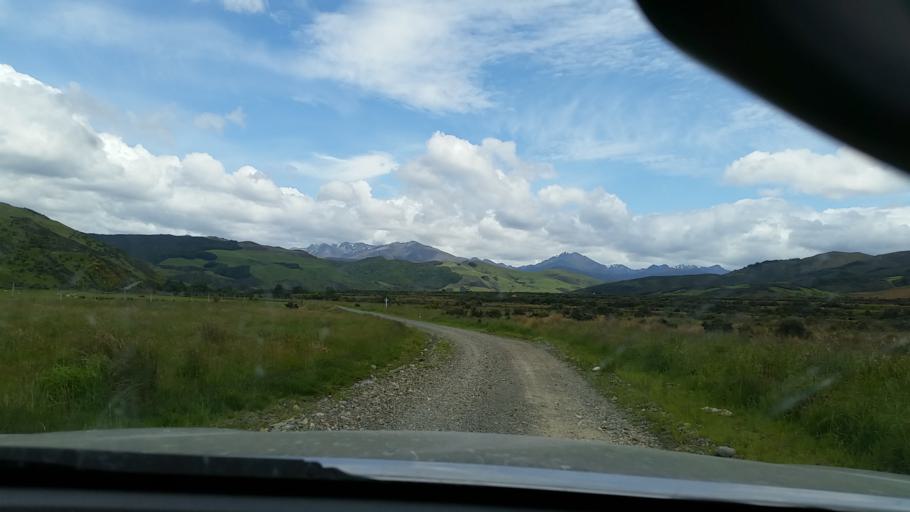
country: NZ
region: Southland
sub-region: Southland District
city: Te Anau
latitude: -45.7464
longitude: 168.0554
